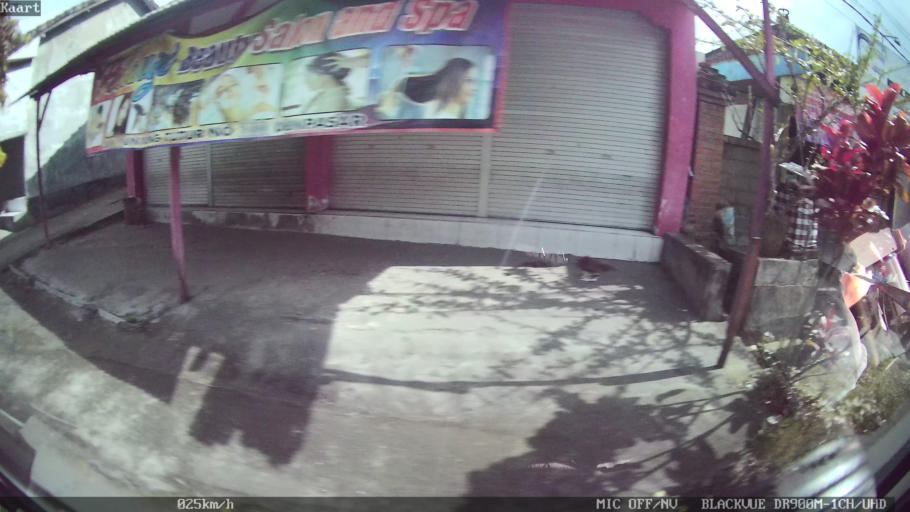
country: ID
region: Bali
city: Banjar Karangsuling
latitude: -8.6112
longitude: 115.2009
